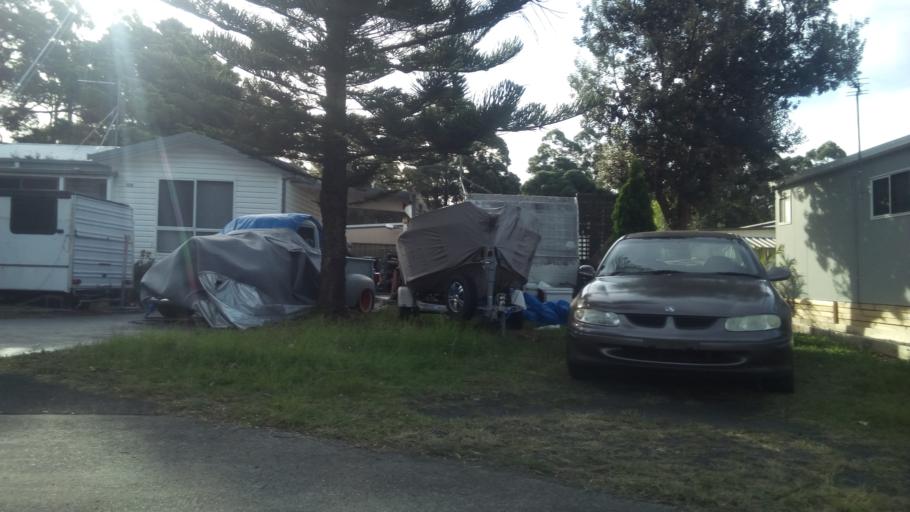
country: AU
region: New South Wales
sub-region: Wollongong
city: Mount Saint Thomas
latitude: -34.4415
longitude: 150.8578
